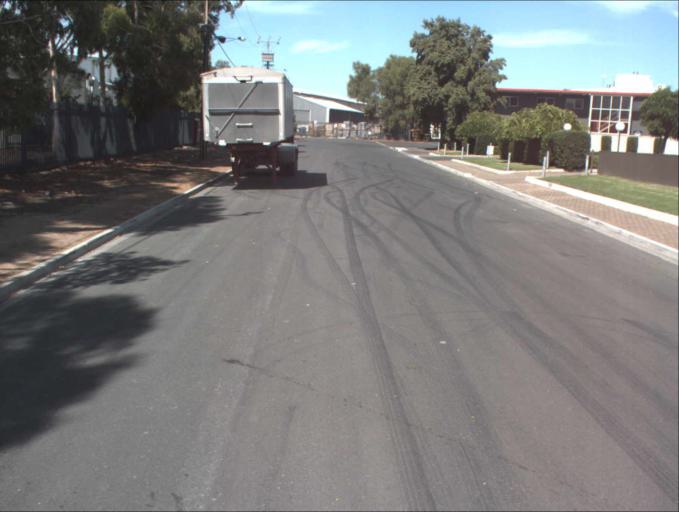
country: AU
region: South Australia
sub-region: Port Adelaide Enfield
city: Gilles Plains
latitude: -34.8651
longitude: 138.6485
